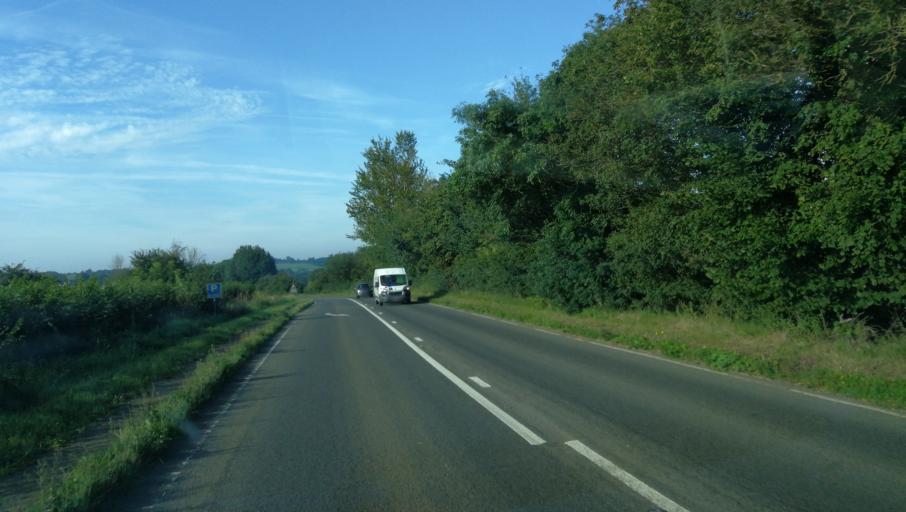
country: GB
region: England
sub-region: Oxfordshire
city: Adderbury
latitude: 52.0040
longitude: -1.3190
